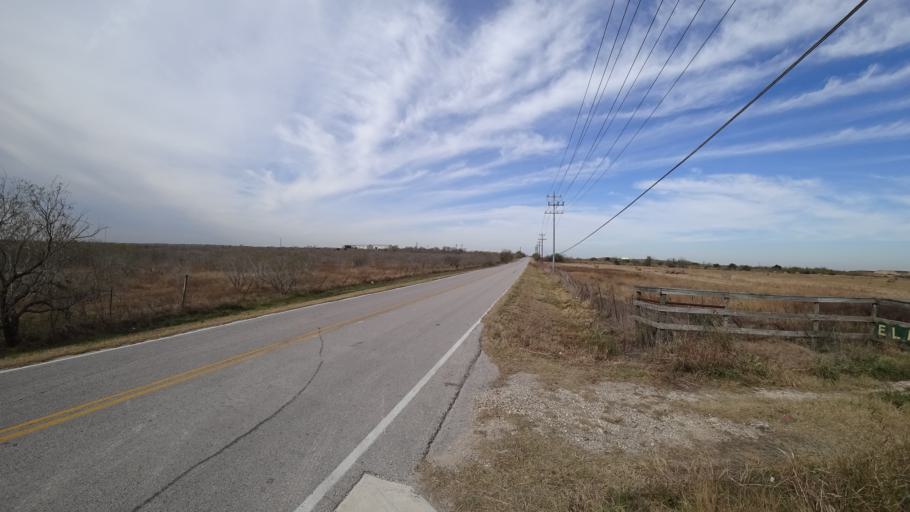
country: US
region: Texas
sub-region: Travis County
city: Onion Creek
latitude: 30.1403
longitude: -97.6829
